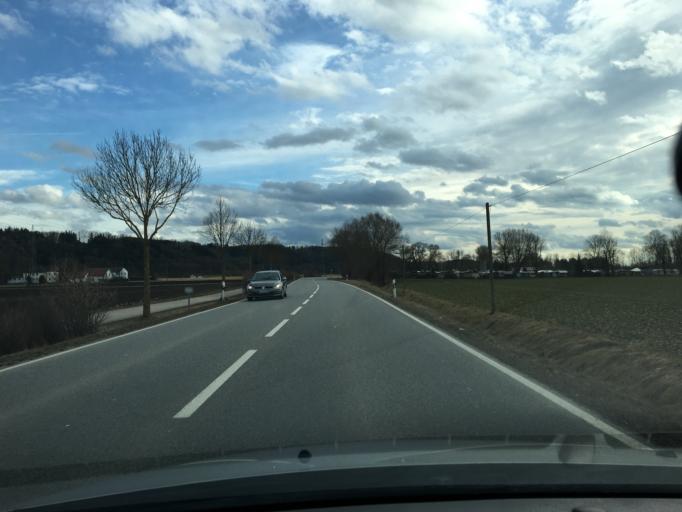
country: DE
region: Bavaria
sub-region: Lower Bavaria
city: Eching
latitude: 48.4831
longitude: 12.0166
